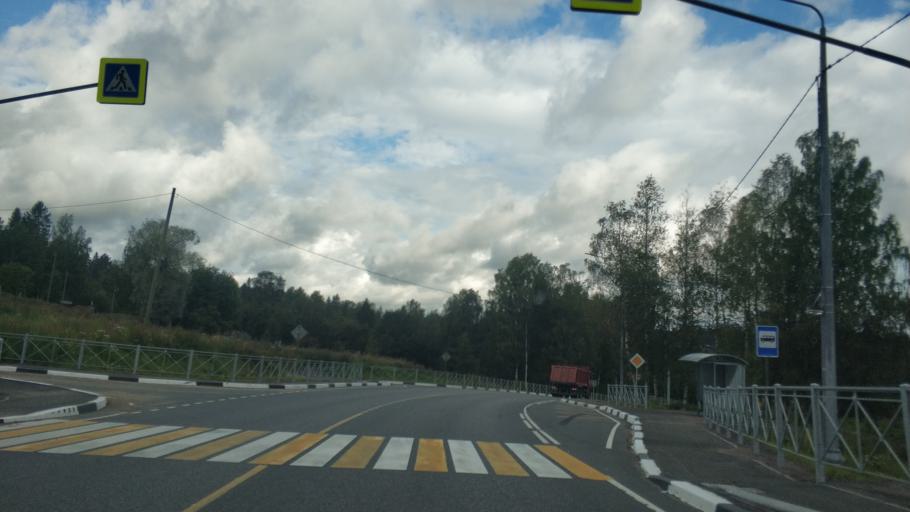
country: RU
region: Republic of Karelia
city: Ruskeala
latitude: 61.9342
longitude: 30.5917
